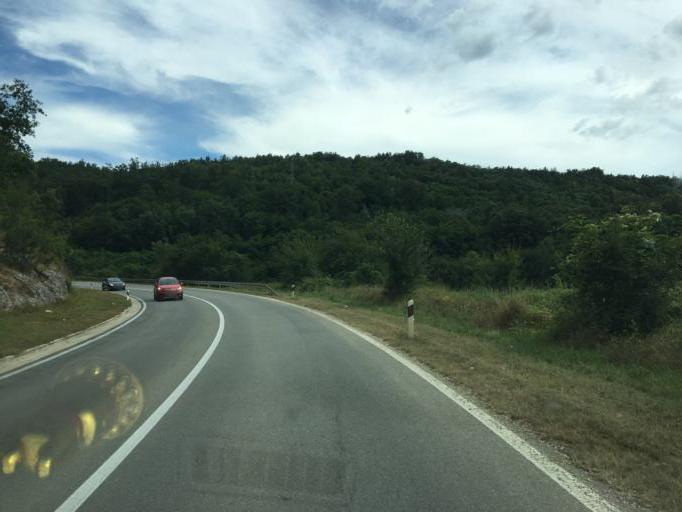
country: HR
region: Istarska
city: Pazin
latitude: 45.2449
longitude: 13.8959
